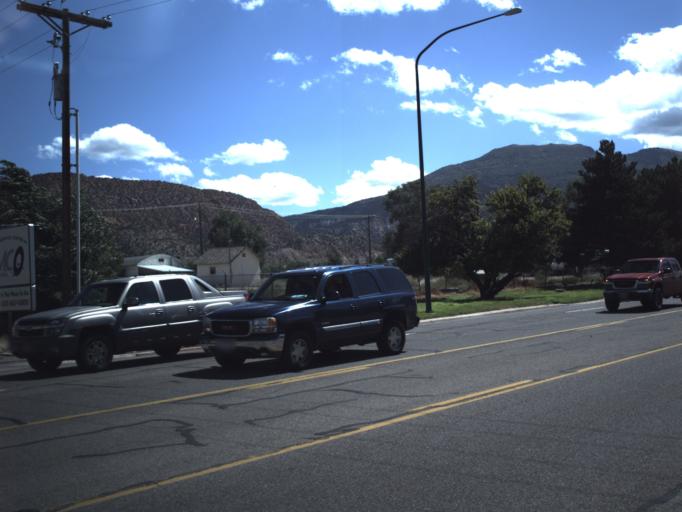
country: US
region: Utah
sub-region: Iron County
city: Cedar City
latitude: 37.6921
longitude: -113.0621
